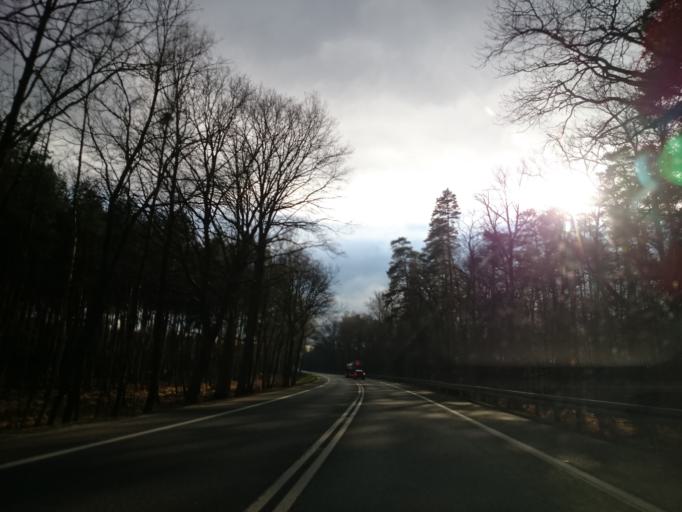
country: PL
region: Opole Voivodeship
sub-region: Powiat opolski
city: Dabrowa
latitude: 50.6737
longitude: 17.7070
